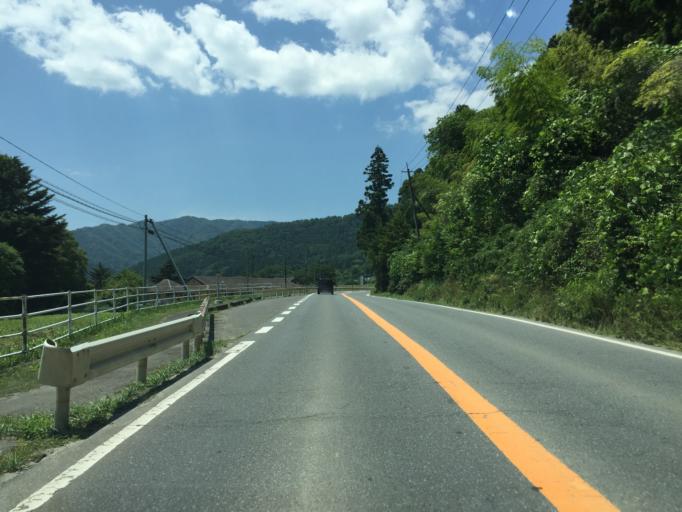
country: JP
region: Miyagi
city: Marumori
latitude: 37.7748
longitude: 140.8677
